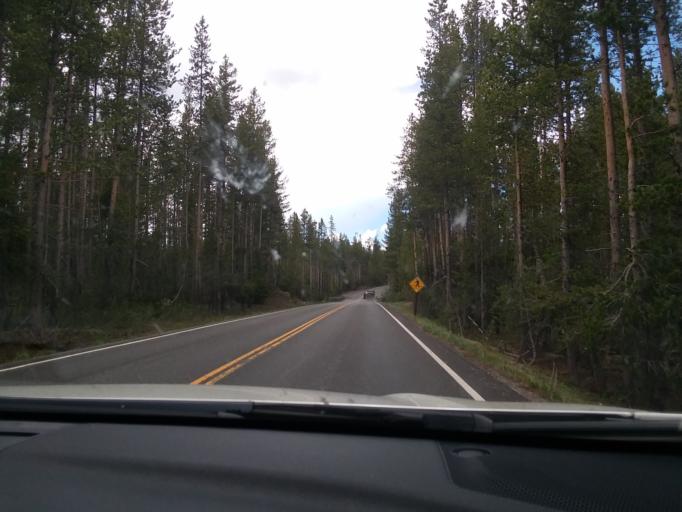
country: US
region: Idaho
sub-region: Teton County
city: Driggs
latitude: 44.1509
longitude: -110.6722
